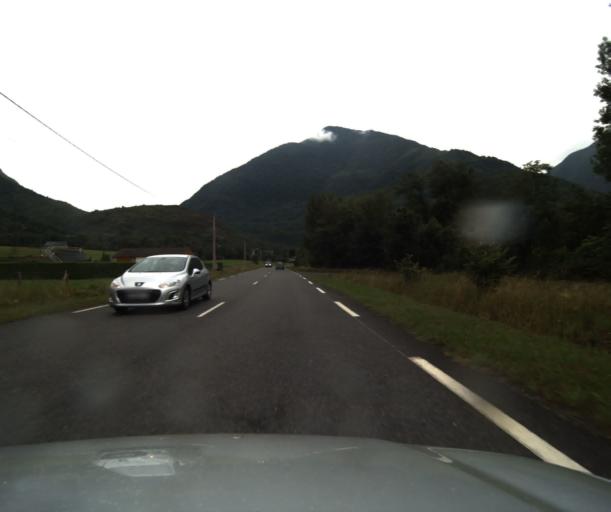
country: FR
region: Midi-Pyrenees
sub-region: Departement des Hautes-Pyrenees
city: Pierrefitte-Nestalas
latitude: 42.9615
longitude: -0.0629
